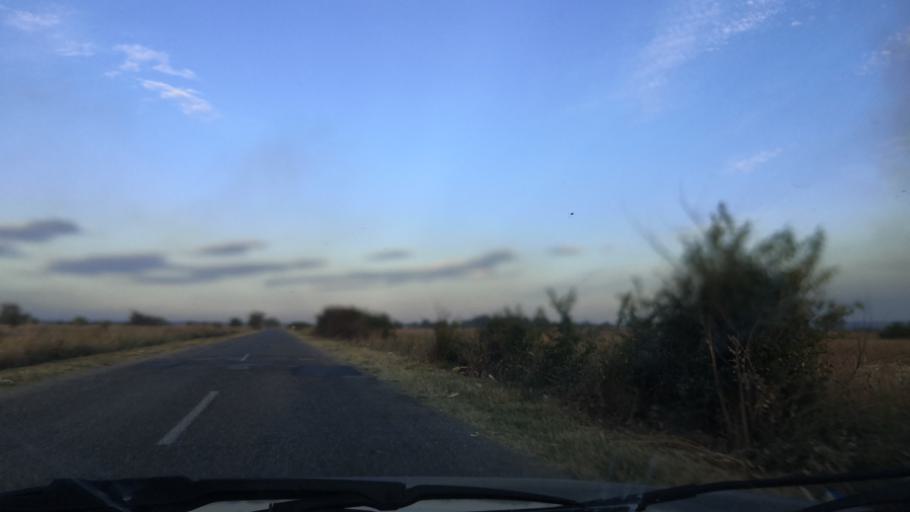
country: RS
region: Central Serbia
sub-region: Borski Okrug
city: Negotin
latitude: 44.2508
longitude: 22.5955
